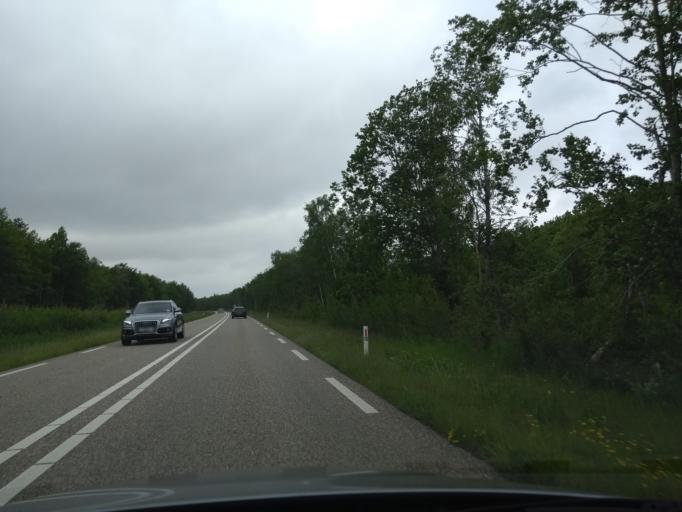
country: NL
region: Friesland
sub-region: Gemeente Dongeradeel
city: Anjum
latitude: 53.4006
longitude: 6.2319
